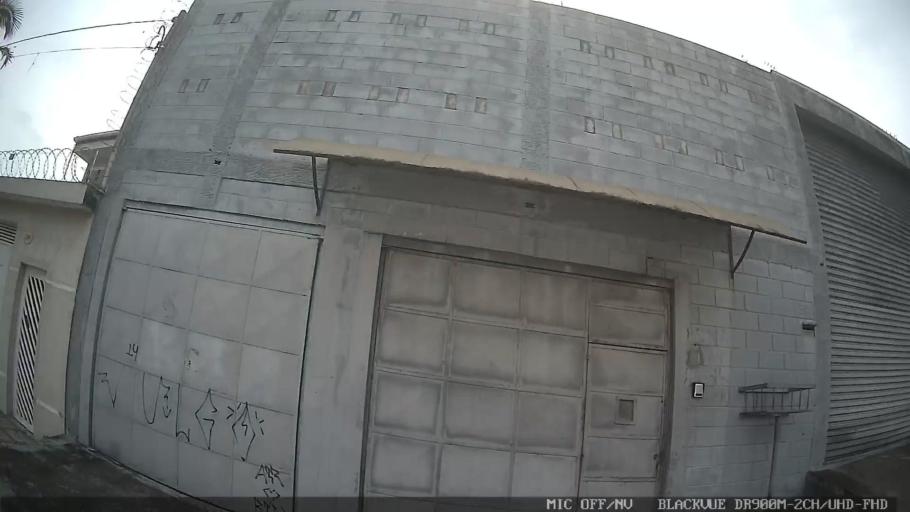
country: BR
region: Sao Paulo
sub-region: Poa
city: Poa
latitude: -23.5208
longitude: -46.3497
